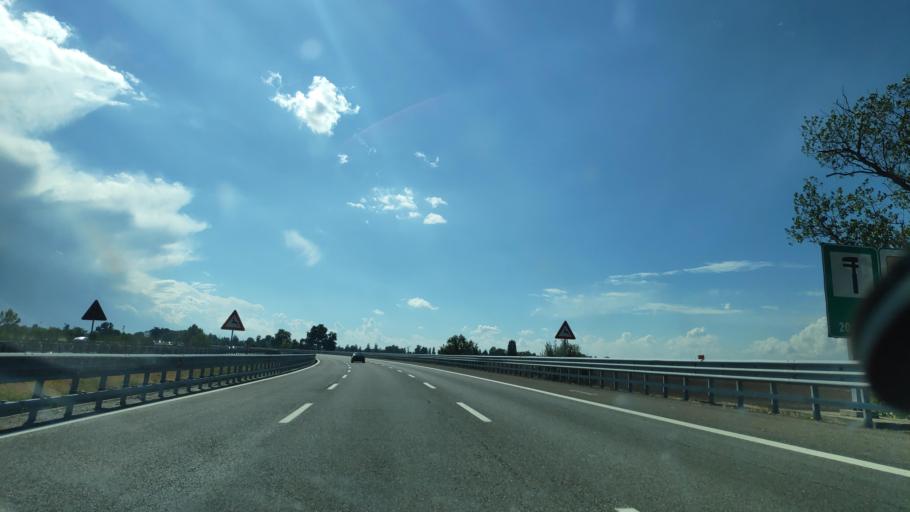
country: IT
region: Piedmont
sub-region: Provincia di Alessandria
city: Castelnuovo Scrivia
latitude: 44.9511
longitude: 8.8649
